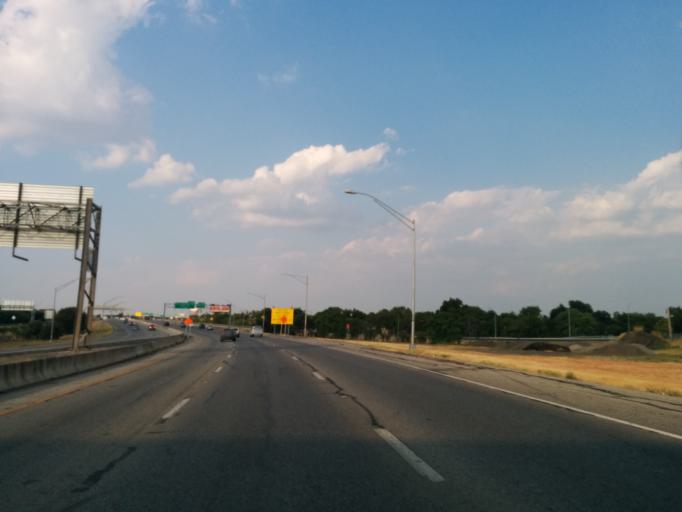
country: US
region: Texas
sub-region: Bexar County
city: San Antonio
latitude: 29.3952
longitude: -98.4778
